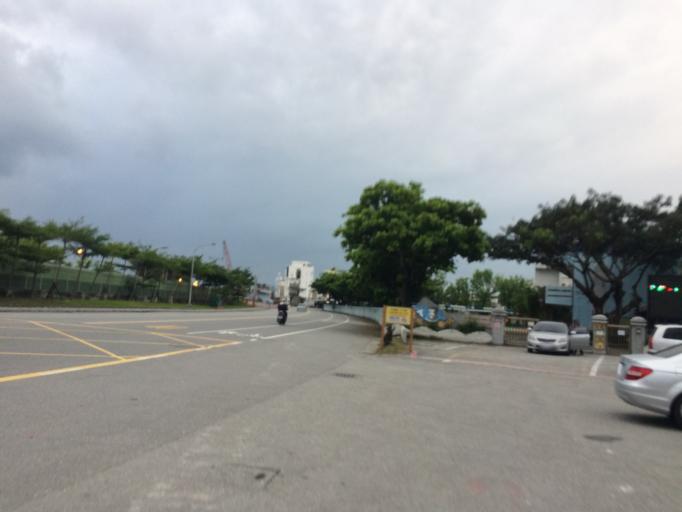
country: TW
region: Taiwan
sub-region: Hualien
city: Hualian
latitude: 23.9786
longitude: 121.6169
